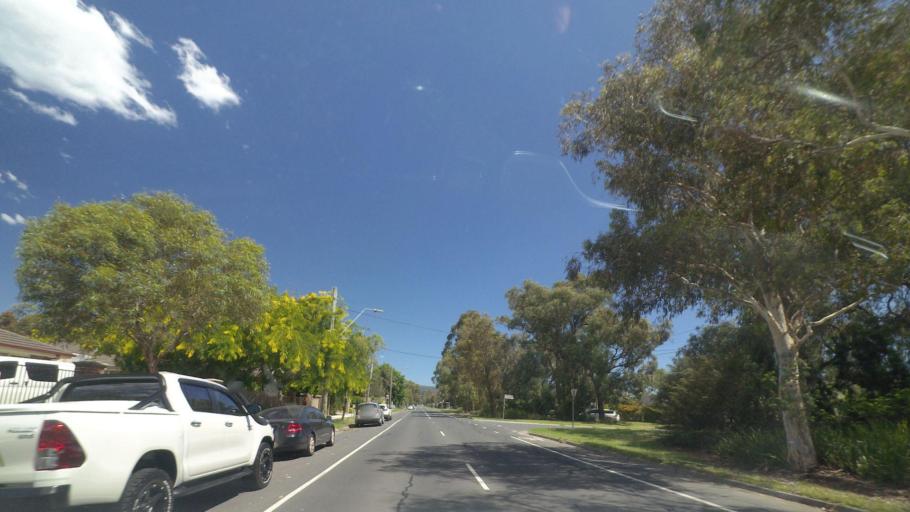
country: AU
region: Victoria
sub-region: Yarra Ranges
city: Kilsyth
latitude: -37.8099
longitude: 145.3157
